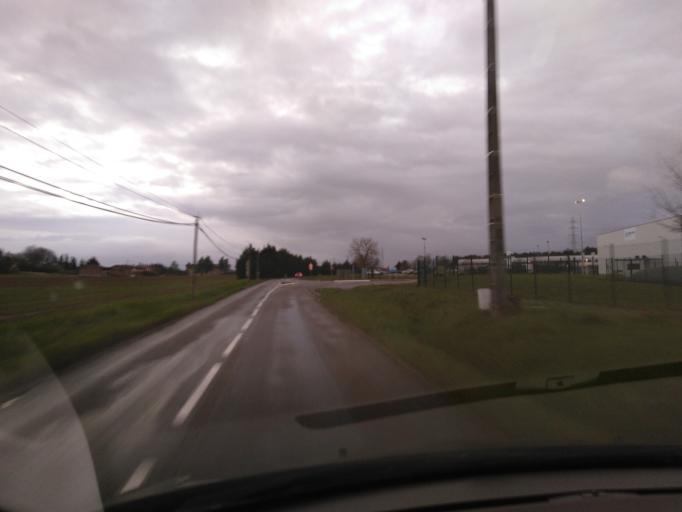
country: FR
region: Midi-Pyrenees
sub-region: Departement de la Haute-Garonne
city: Seilh
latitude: 43.6802
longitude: 1.3436
